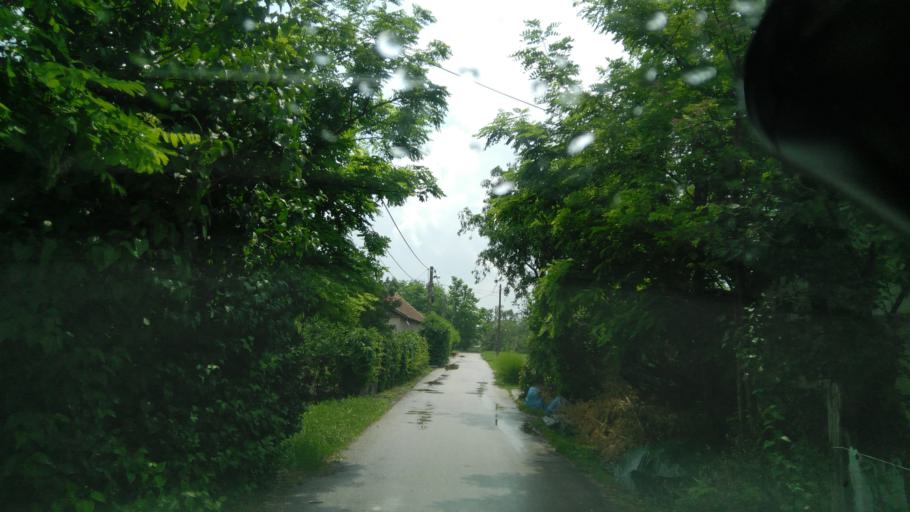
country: HU
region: Bekes
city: Bekescsaba
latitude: 46.6608
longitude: 21.1700
